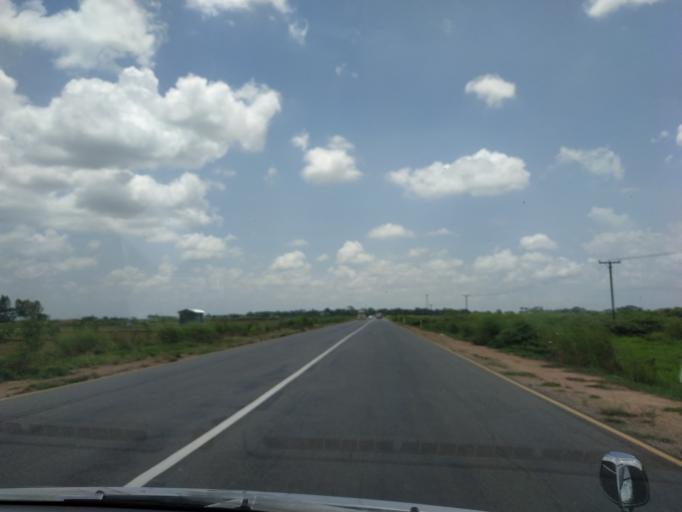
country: MM
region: Bago
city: Bago
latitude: 17.4684
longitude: 96.5698
